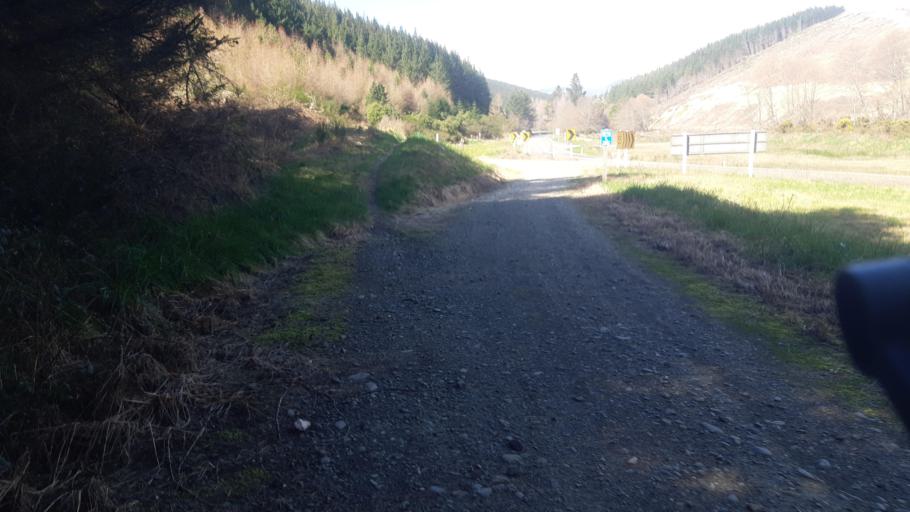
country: NZ
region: Tasman
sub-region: Tasman District
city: Wakefield
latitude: -41.4831
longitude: 172.8855
